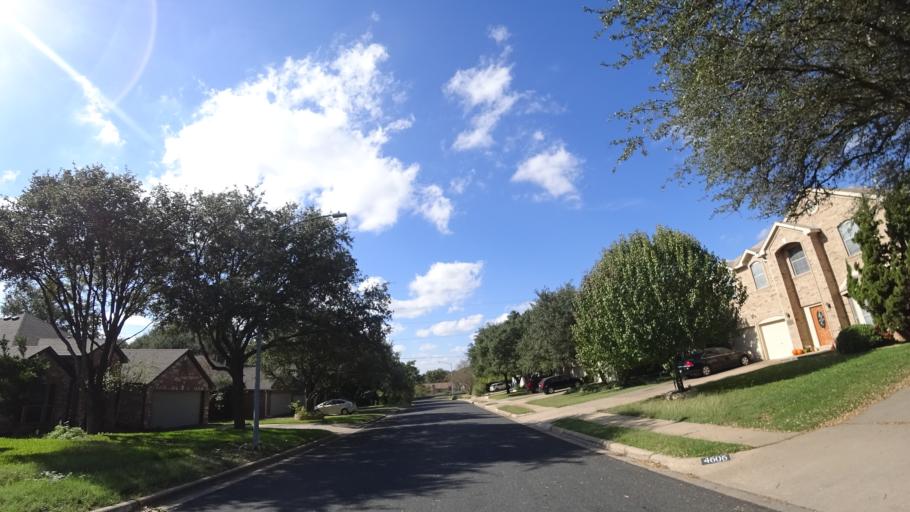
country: US
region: Texas
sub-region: Williamson County
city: Jollyville
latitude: 30.4201
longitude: -97.7285
